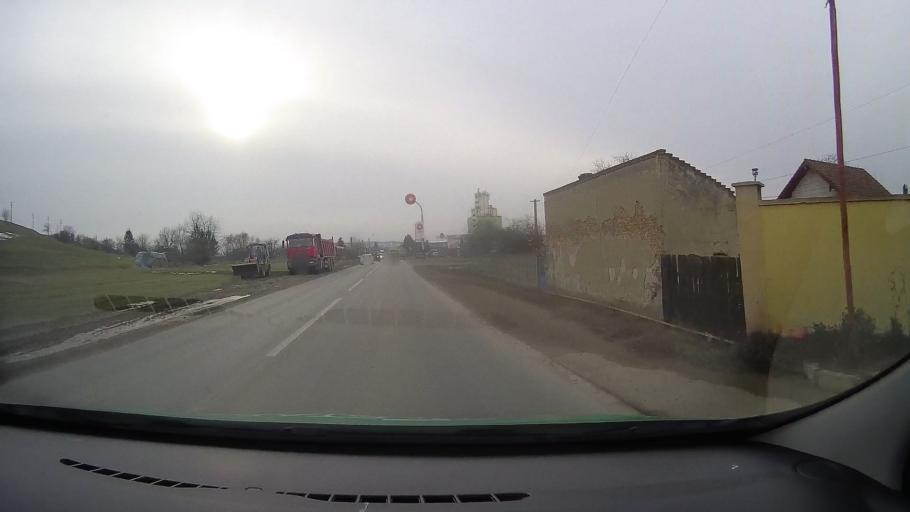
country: RO
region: Hunedoara
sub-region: Municipiul Orastie
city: Orastie
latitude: 45.8616
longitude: 23.2167
